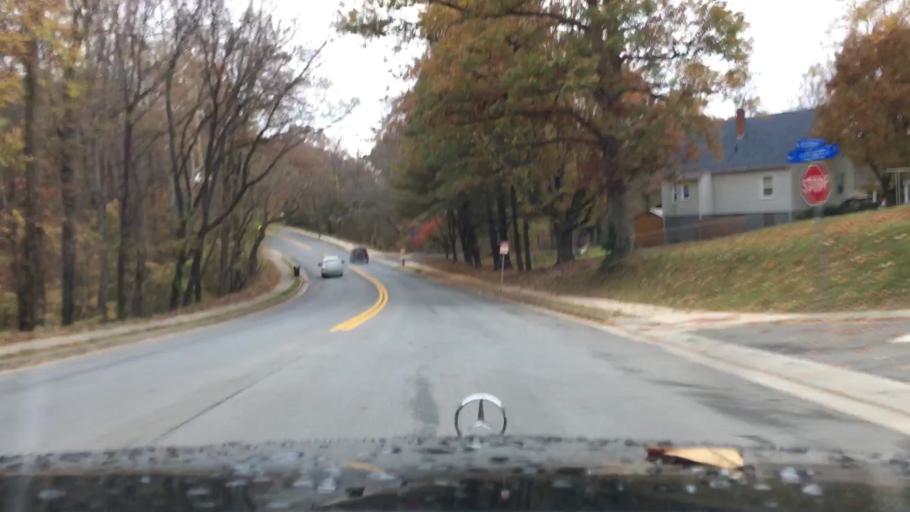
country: US
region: Virginia
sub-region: Campbell County
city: Altavista
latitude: 37.1183
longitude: -79.3016
